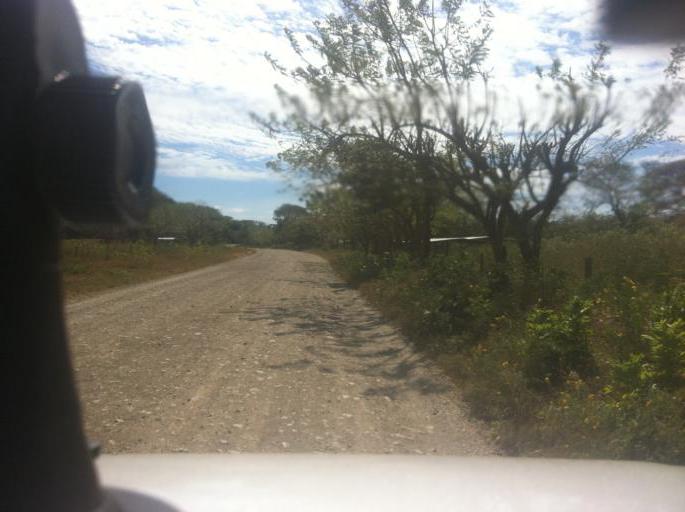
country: NI
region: Rivas
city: Tola
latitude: 11.5225
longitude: -86.0694
